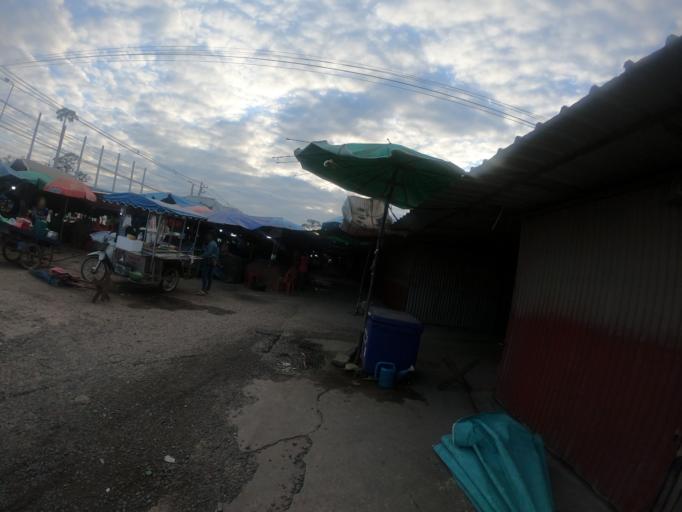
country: TH
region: Surin
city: Kap Choeng
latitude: 14.4541
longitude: 103.6884
